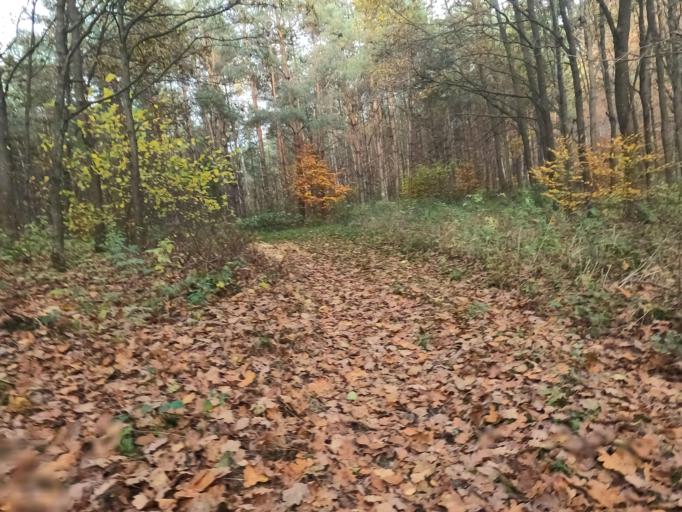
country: PL
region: Pomeranian Voivodeship
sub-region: Powiat starogardzki
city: Skarszewy
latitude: 54.0096
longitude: 18.4587
